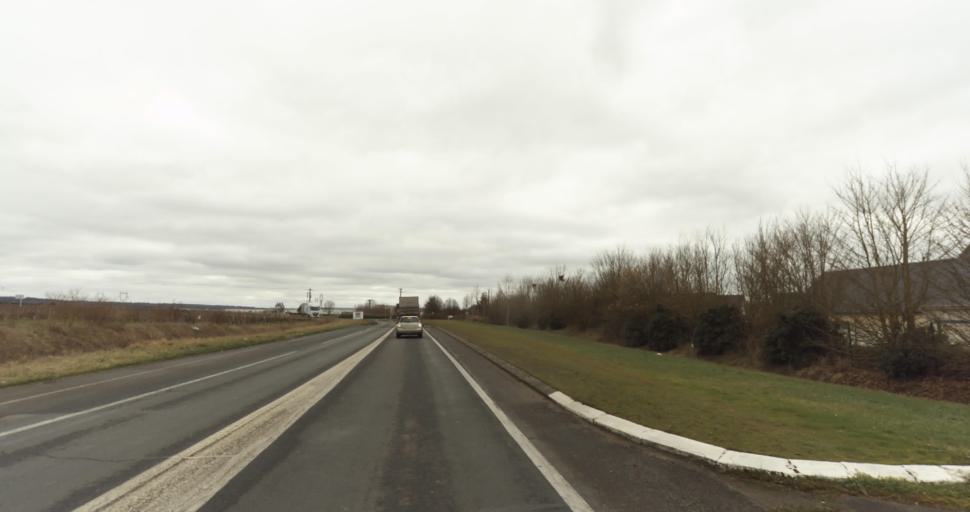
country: FR
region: Pays de la Loire
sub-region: Departement de Maine-et-Loire
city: Varrains
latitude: 47.2152
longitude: -0.0596
